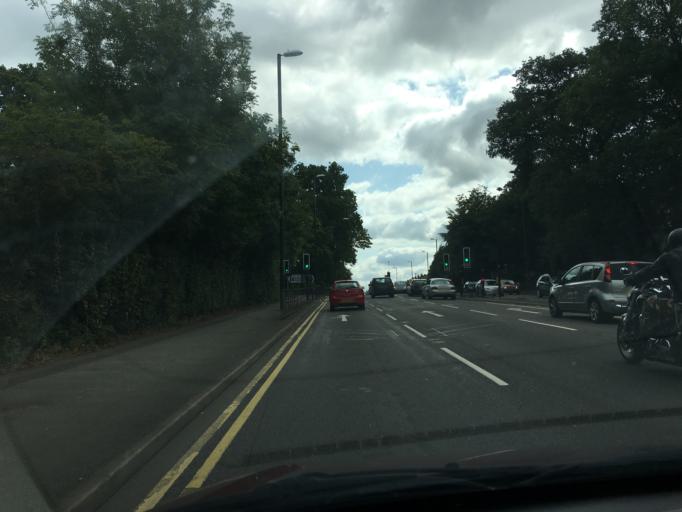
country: GB
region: England
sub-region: Coventry
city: Coventry
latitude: 52.3868
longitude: -1.5361
